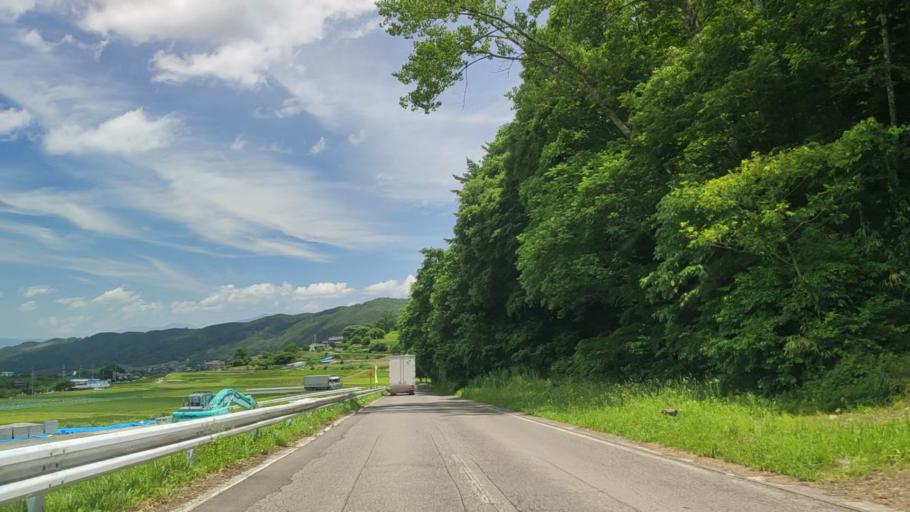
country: JP
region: Nagano
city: Kamimaruko
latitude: 36.2409
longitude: 138.2578
